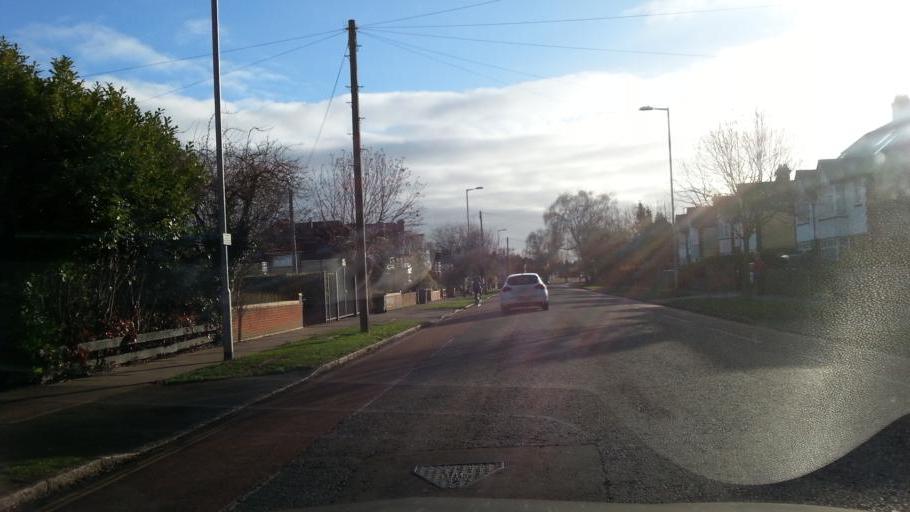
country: GB
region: England
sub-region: Cambridgeshire
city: Cambridge
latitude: 52.2186
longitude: 0.1234
